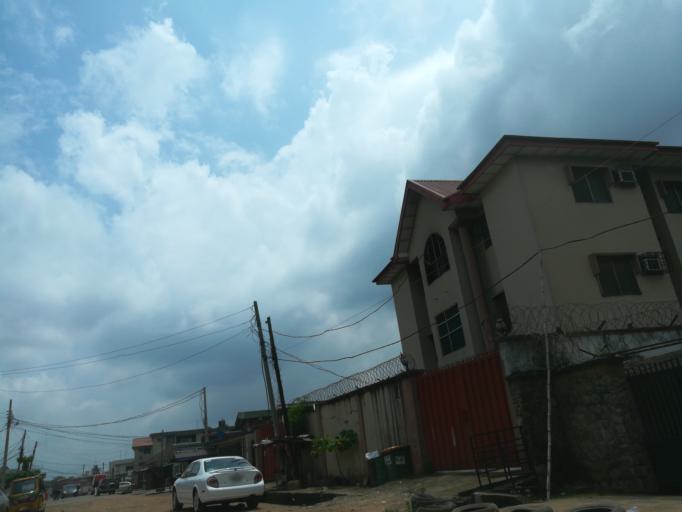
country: NG
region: Lagos
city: Oshodi
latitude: 6.5480
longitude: 3.3268
